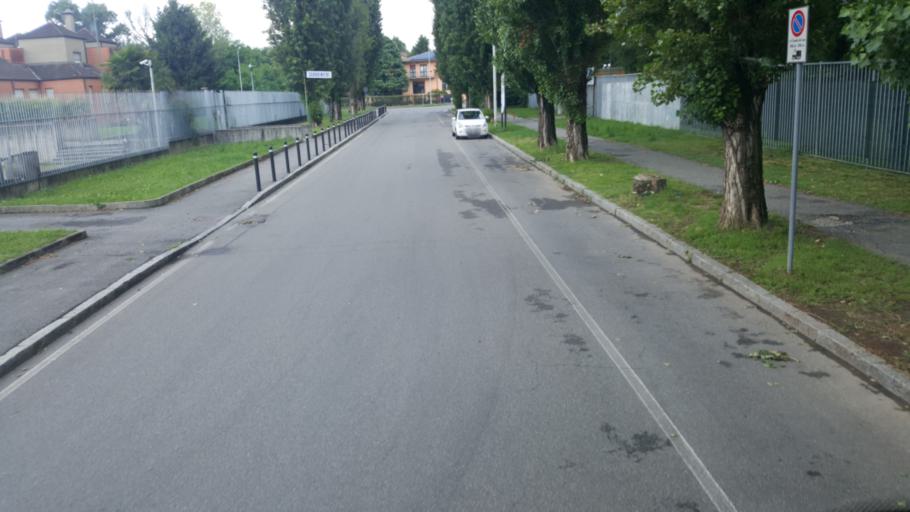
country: IT
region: Lombardy
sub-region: Citta metropolitana di Milano
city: Melzo
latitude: 45.4951
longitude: 9.4164
